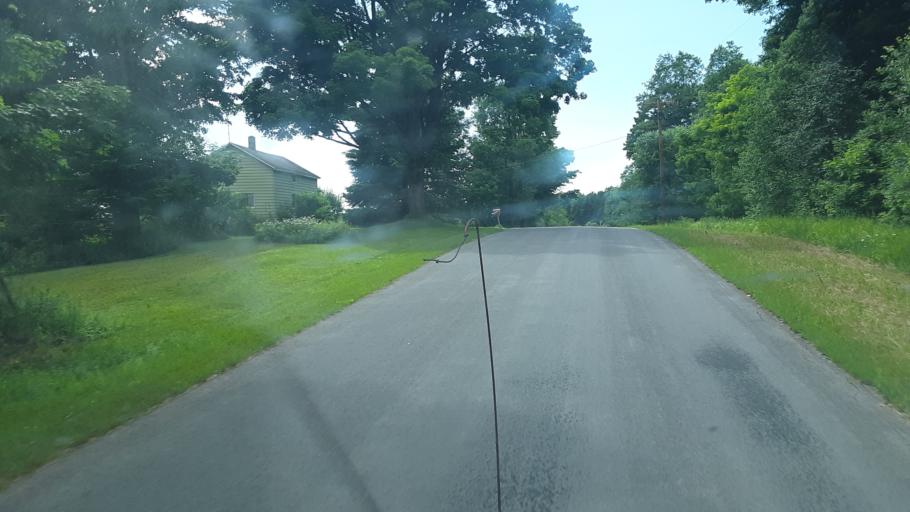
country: US
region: New York
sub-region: Oneida County
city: Rome
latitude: 43.3928
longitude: -75.5001
